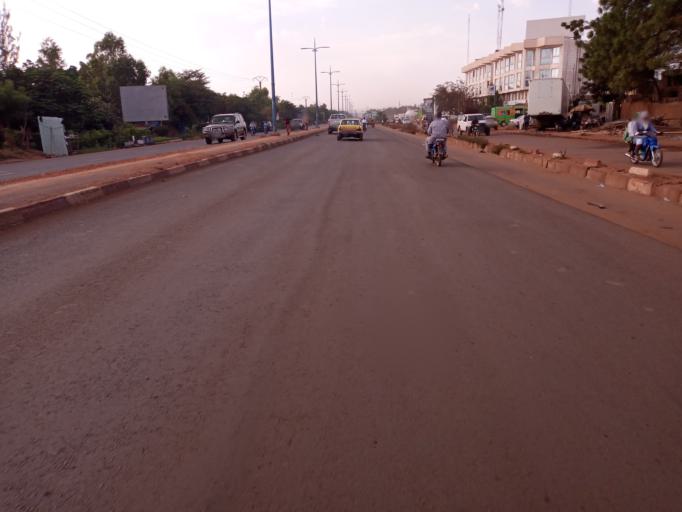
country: ML
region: Bamako
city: Bamako
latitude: 12.5865
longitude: -7.9458
